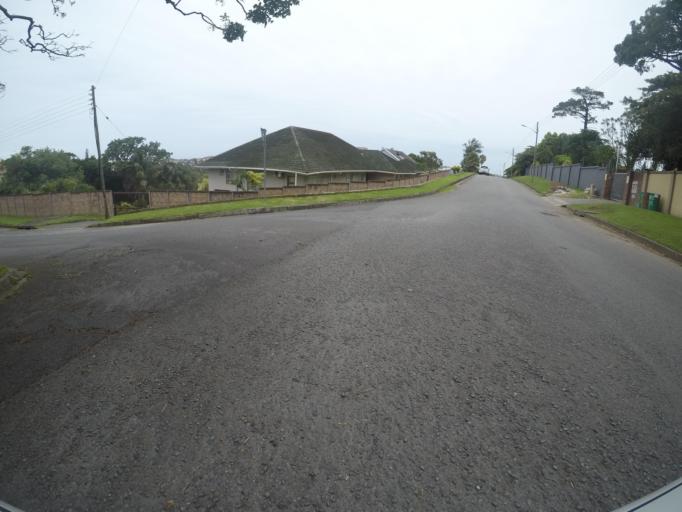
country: ZA
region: Eastern Cape
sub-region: Buffalo City Metropolitan Municipality
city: East London
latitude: -32.9766
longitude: 27.9384
